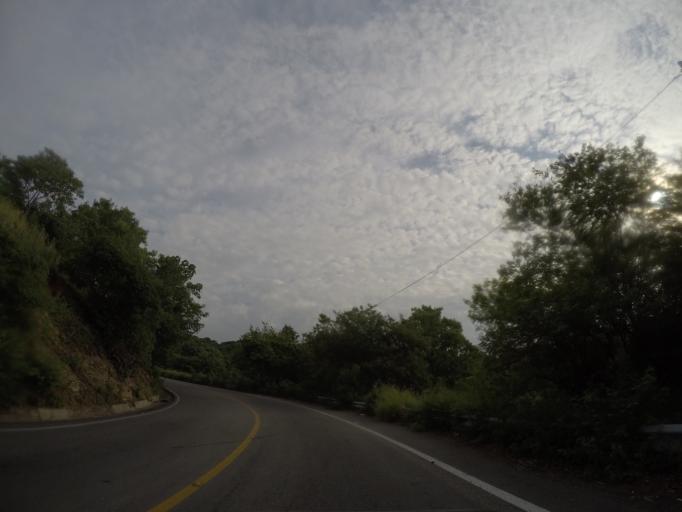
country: MX
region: Oaxaca
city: San Pedro Pochutla
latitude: 15.7015
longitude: -96.4817
